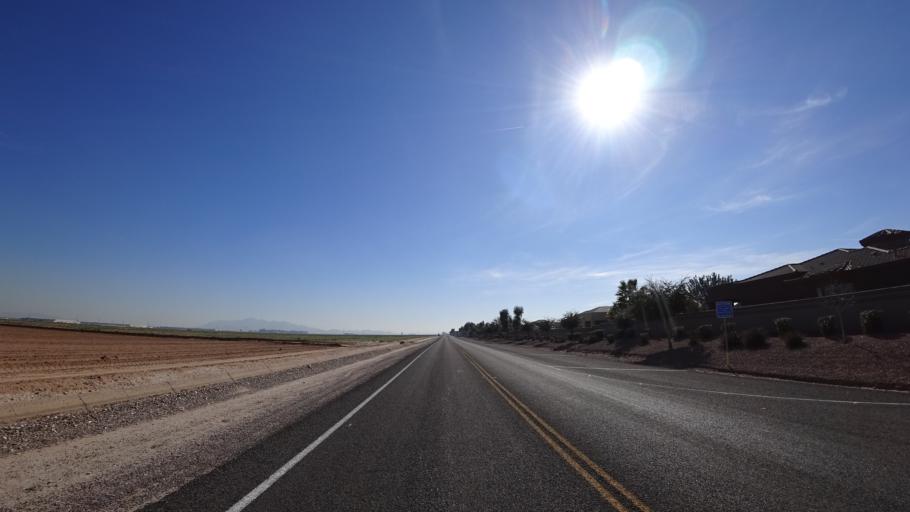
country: US
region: Arizona
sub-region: Maricopa County
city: Citrus Park
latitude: 33.5197
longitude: -112.4442
